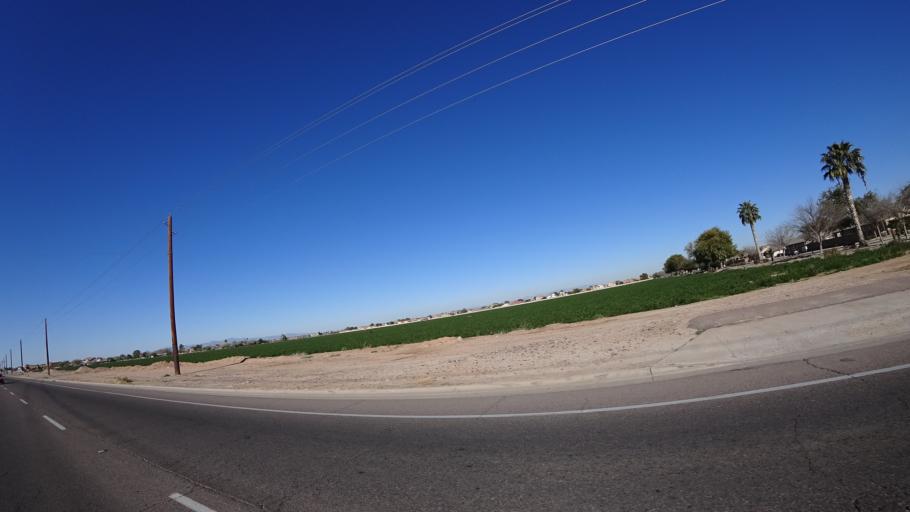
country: US
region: Arizona
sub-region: Maricopa County
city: Laveen
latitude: 33.3777
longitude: -112.1274
